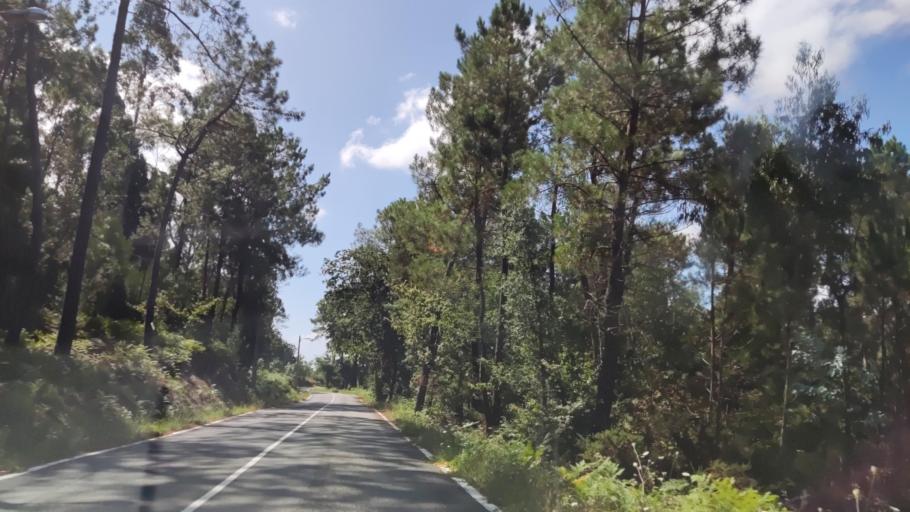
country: ES
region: Galicia
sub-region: Provincia da Coruna
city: Rianxo
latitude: 42.6922
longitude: -8.8428
